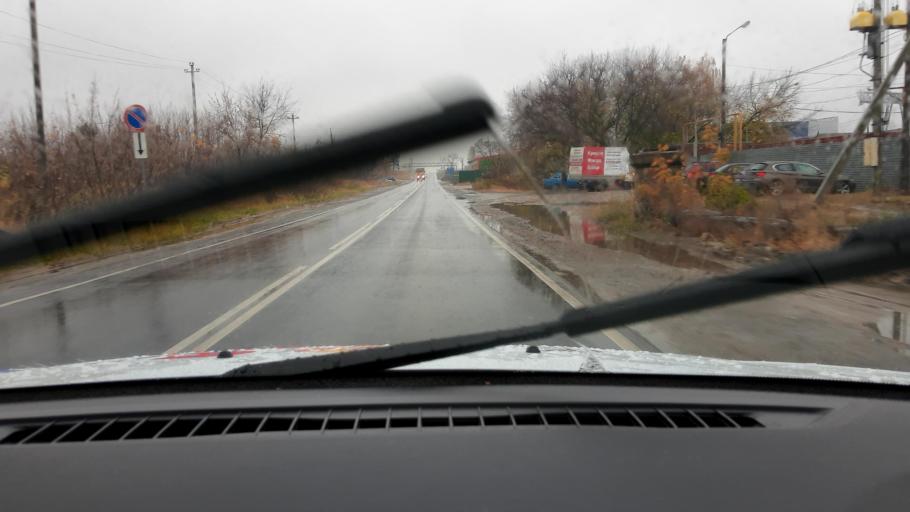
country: RU
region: Nizjnij Novgorod
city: Babino
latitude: 56.2619
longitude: 43.5935
